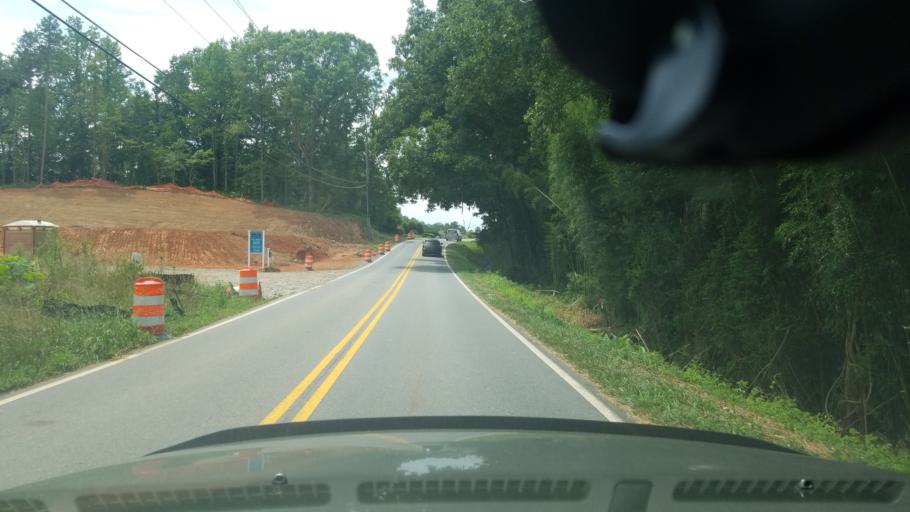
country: US
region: Georgia
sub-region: Fulton County
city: Milton
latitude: 34.1933
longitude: -84.2392
